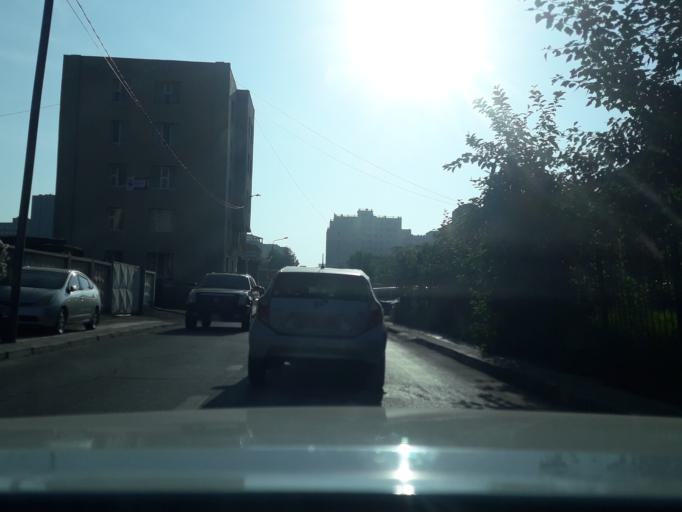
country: MN
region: Ulaanbaatar
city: Ulaanbaatar
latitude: 47.8961
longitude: 106.9031
